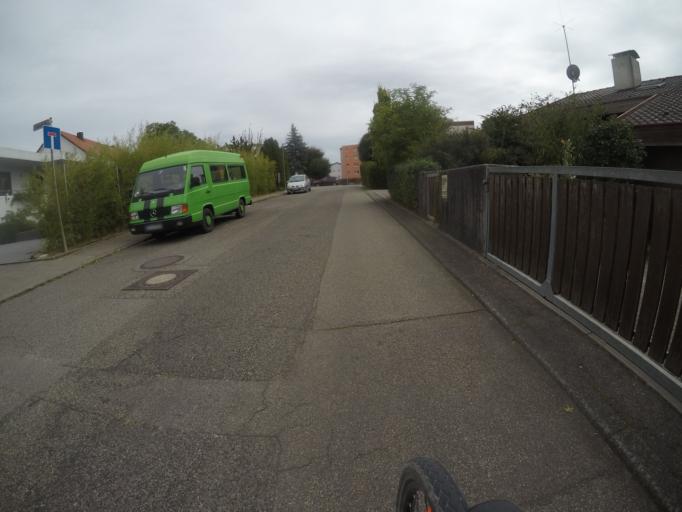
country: DE
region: Baden-Wuerttemberg
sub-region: Regierungsbezirk Stuttgart
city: Vaihingen an der Enz
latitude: 48.9509
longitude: 8.9768
